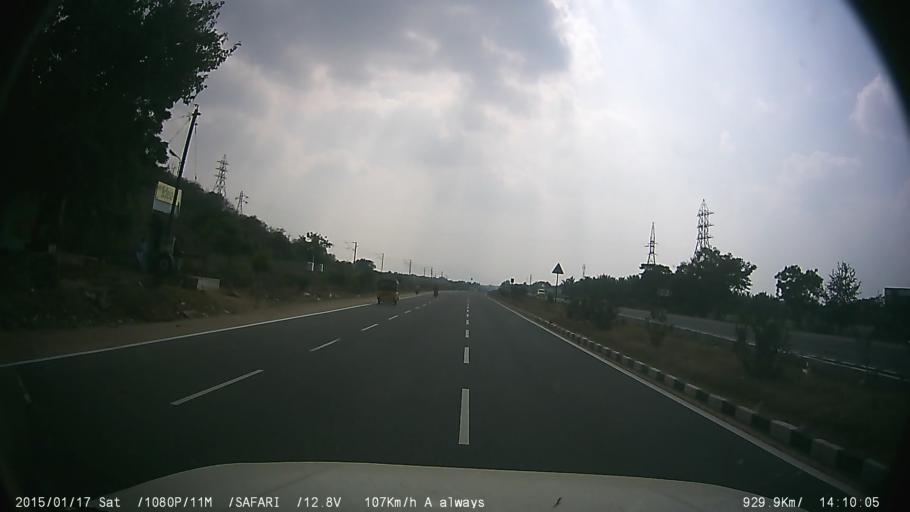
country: IN
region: Tamil Nadu
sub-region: Vellore
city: Ambur
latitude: 12.8106
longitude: 78.7412
